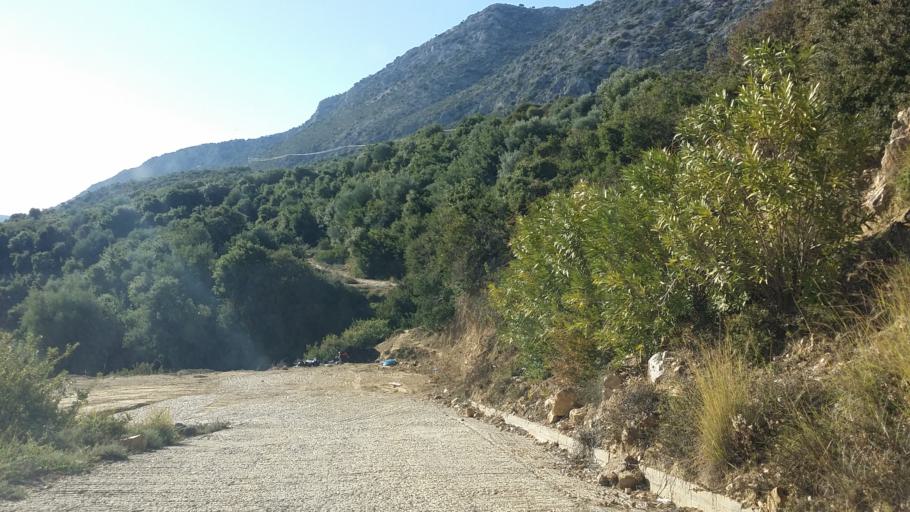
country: GR
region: West Greece
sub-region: Nomos Aitolias kai Akarnanias
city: Astakos
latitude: 38.5226
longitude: 21.0668
